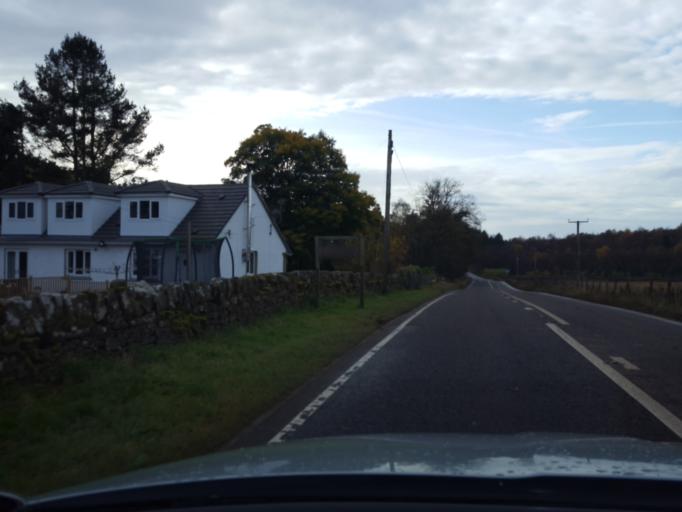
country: GB
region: Scotland
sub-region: South Lanarkshire
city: Carnwath
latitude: 55.7135
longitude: -3.5937
